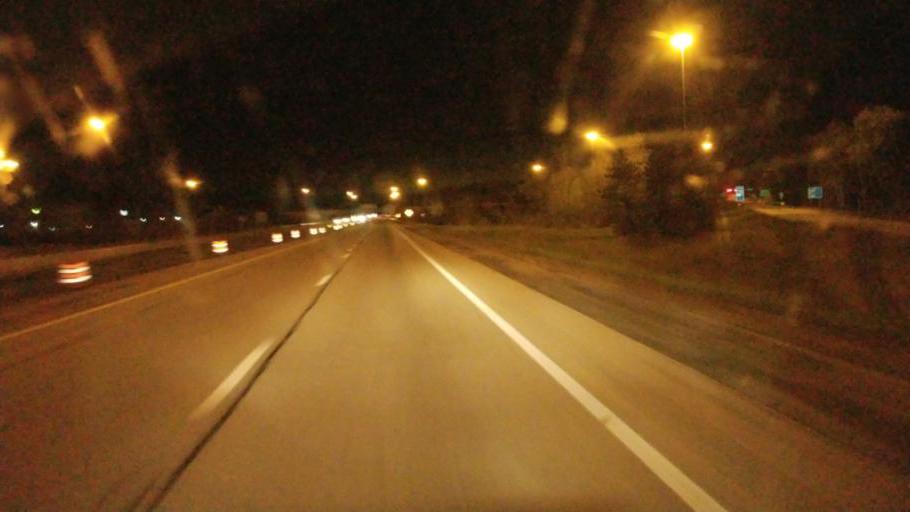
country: US
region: Ohio
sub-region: Licking County
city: Buckeye Lake
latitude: 39.9458
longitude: -82.4754
